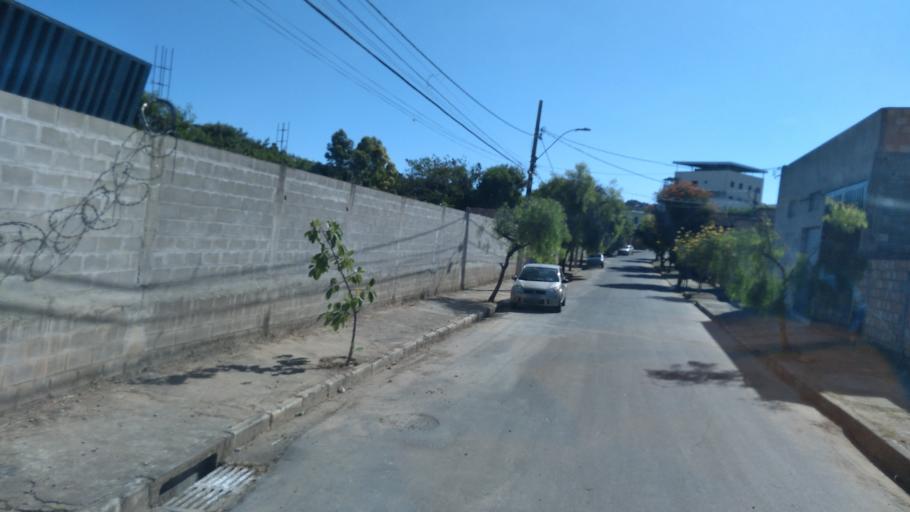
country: BR
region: Minas Gerais
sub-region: Belo Horizonte
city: Belo Horizonte
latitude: -19.8436
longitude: -43.9059
